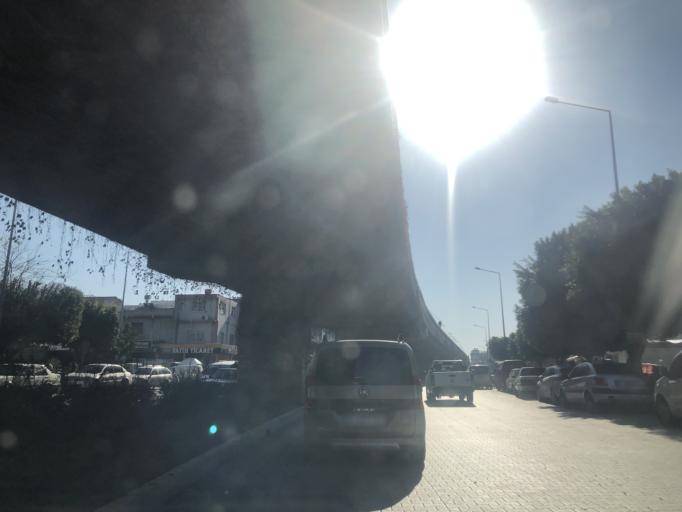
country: TR
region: Adana
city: Seyhan
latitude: 36.9838
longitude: 35.3199
